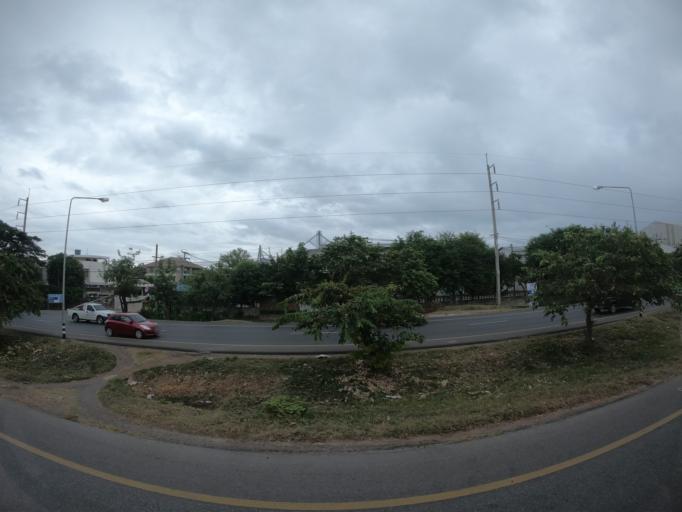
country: TH
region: Roi Et
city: Roi Et
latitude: 16.0587
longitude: 103.6194
